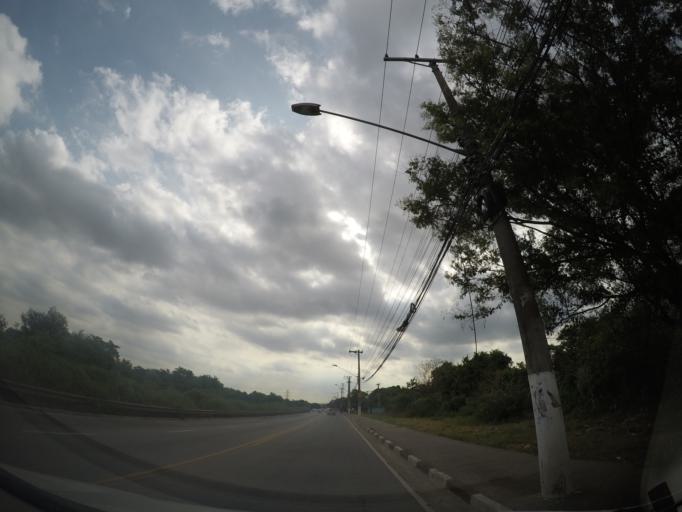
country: BR
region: Sao Paulo
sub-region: Guarulhos
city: Guarulhos
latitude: -23.4177
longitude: -46.4772
